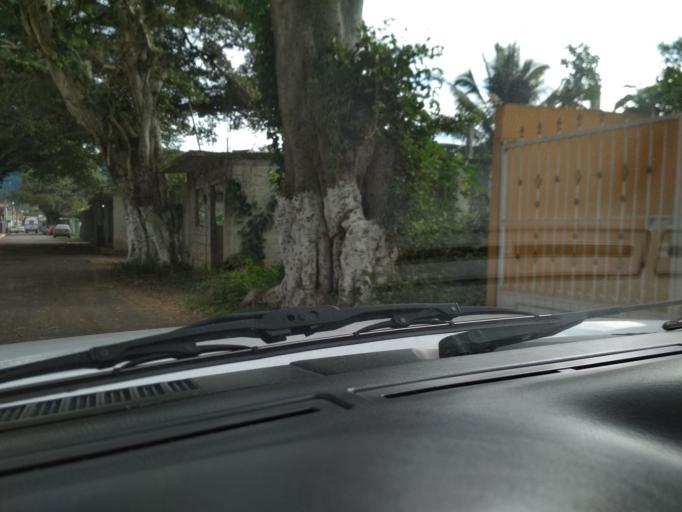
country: MX
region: Veracruz
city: Alto Lucero
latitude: 19.5894
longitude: -96.7856
